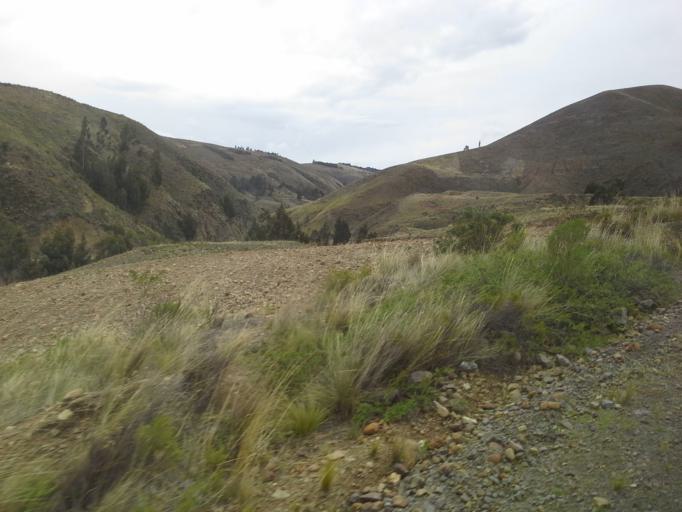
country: BO
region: Cochabamba
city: Colomi
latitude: -17.4026
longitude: -65.8129
